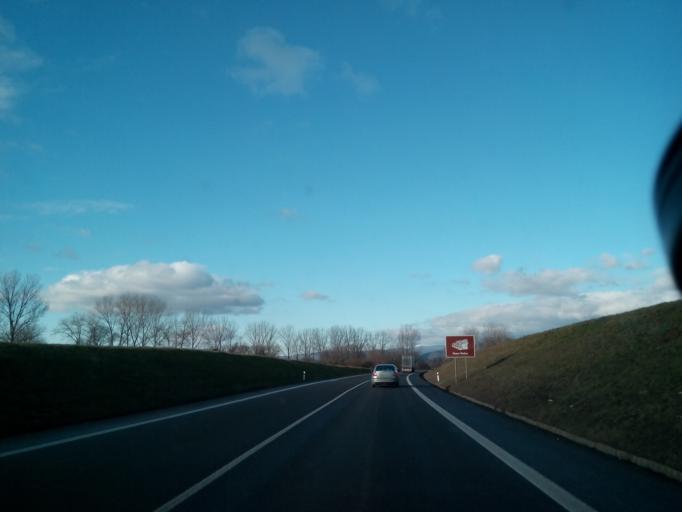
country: SK
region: Kosicky
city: Moldava nad Bodvou
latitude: 48.5983
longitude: 21.0389
